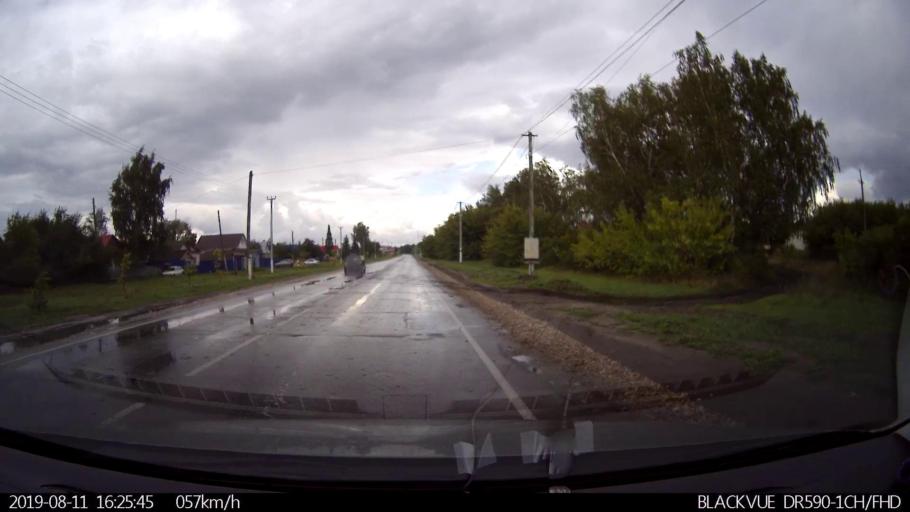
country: RU
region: Ulyanovsk
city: Mayna
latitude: 54.1073
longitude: 47.6086
